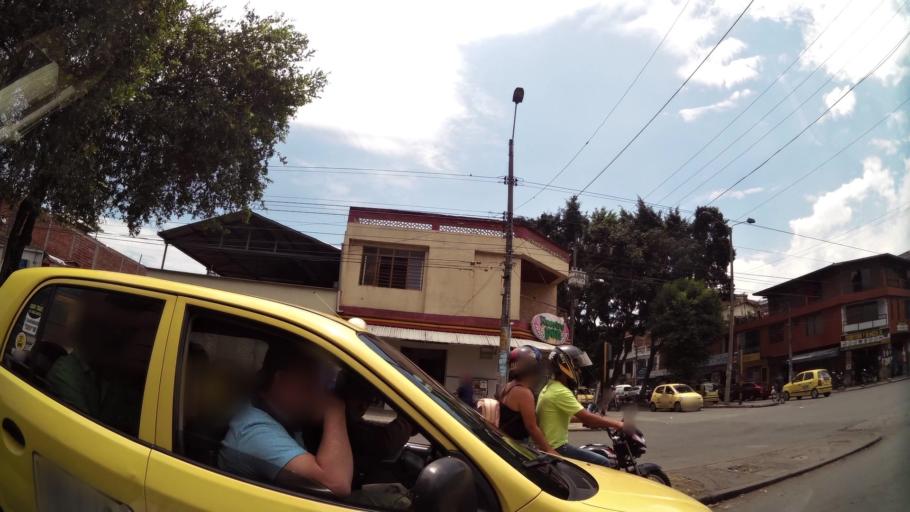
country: CO
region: Valle del Cauca
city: Cali
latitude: 3.4484
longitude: -76.4989
